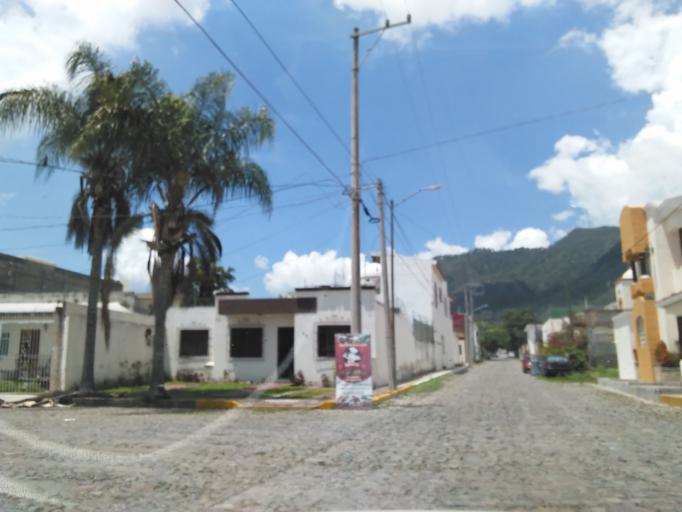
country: MX
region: Nayarit
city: Tepic
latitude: 21.5118
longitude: -104.9144
